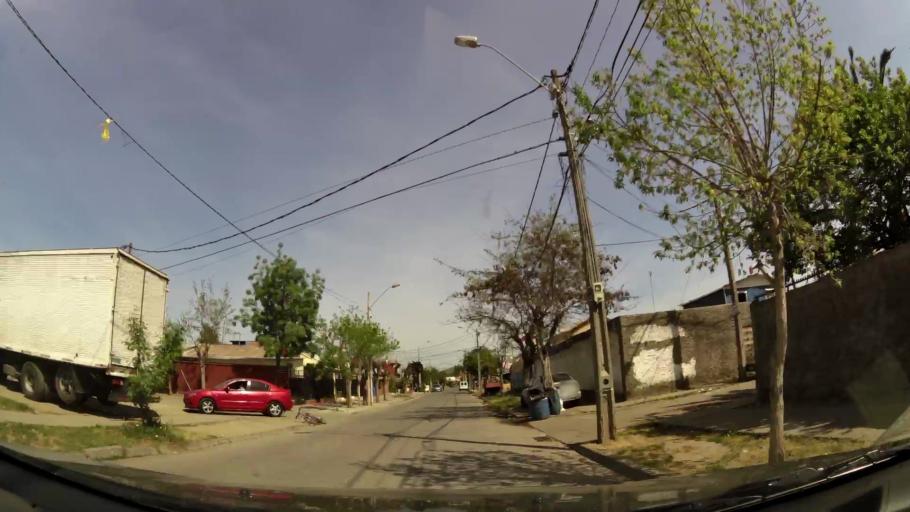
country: CL
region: Santiago Metropolitan
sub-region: Provincia de Cordillera
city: Puente Alto
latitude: -33.6224
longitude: -70.5834
